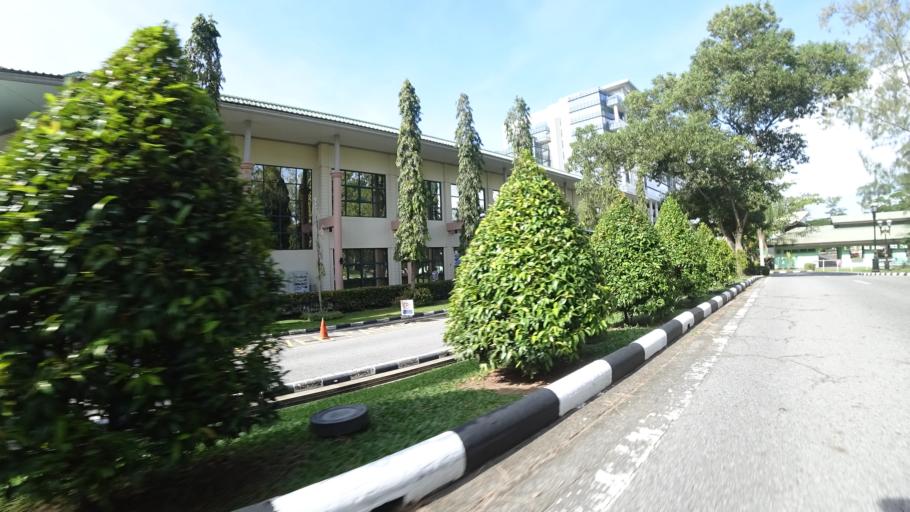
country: BN
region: Brunei and Muara
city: Bandar Seri Begawan
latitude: 4.9485
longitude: 114.8309
